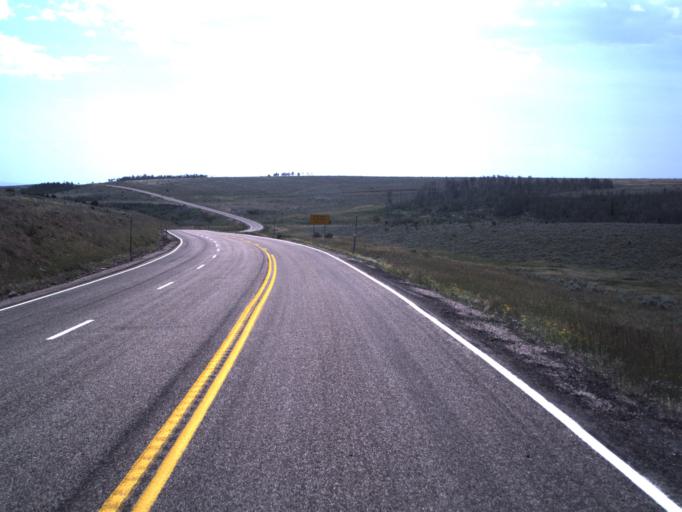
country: US
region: Utah
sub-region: Uintah County
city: Maeser
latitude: 40.6887
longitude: -109.4948
